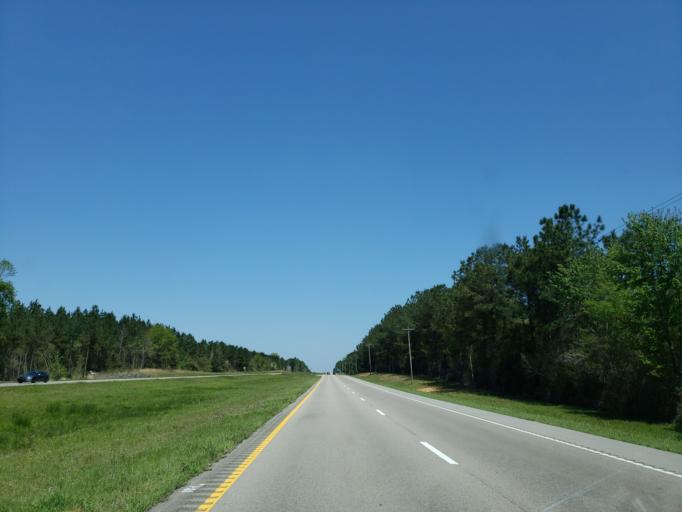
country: US
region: Mississippi
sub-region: Stone County
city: Wiggins
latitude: 31.0151
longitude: -89.2018
